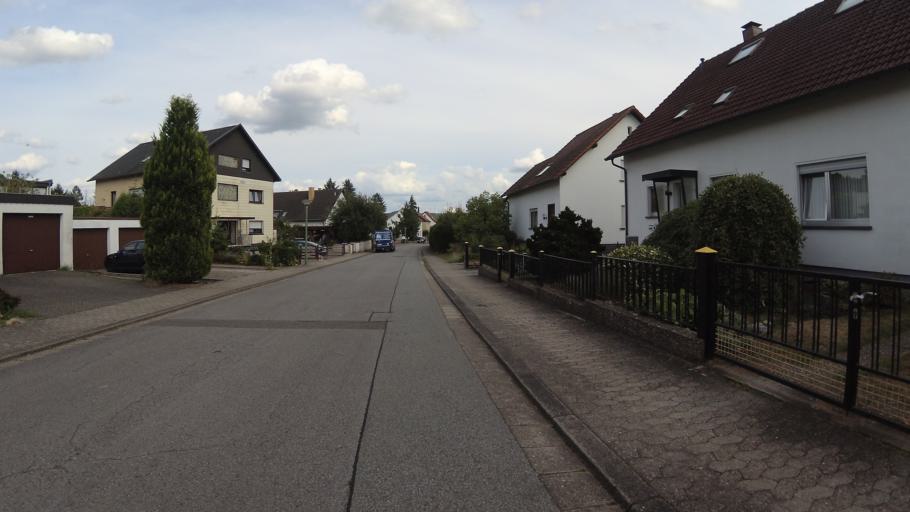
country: DE
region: Saarland
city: Bexbach
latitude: 49.3102
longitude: 7.2877
